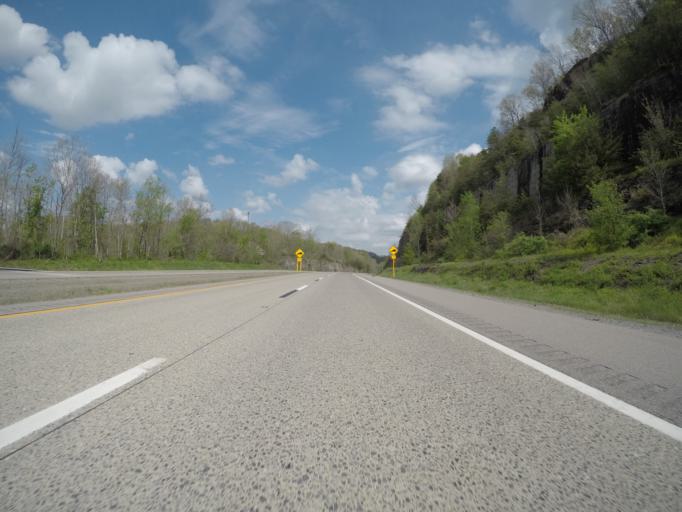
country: US
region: West Virginia
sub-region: Kanawha County
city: Alum Creek
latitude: 38.2171
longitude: -81.8330
